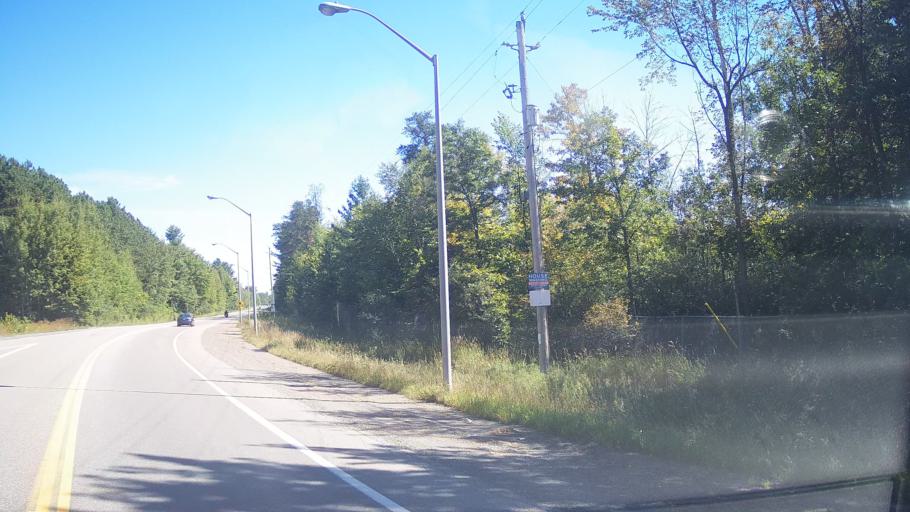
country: CA
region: Ontario
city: Bells Corners
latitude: 45.0543
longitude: -75.6823
